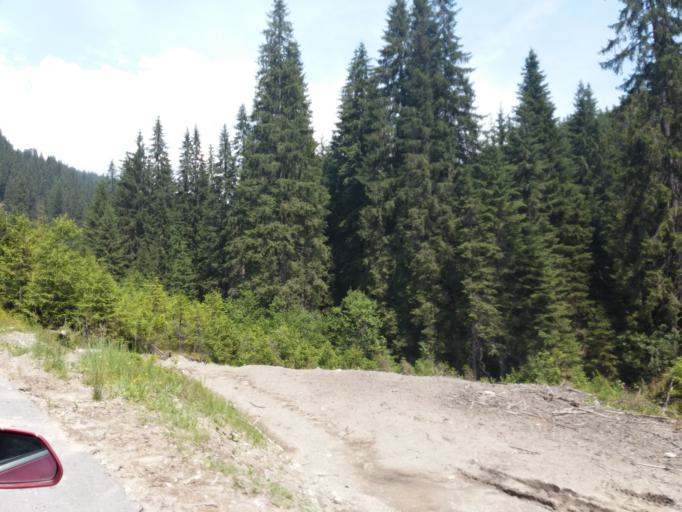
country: RO
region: Valcea
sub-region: Comuna Voineasa
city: Voineasa
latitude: 45.4243
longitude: 23.7798
